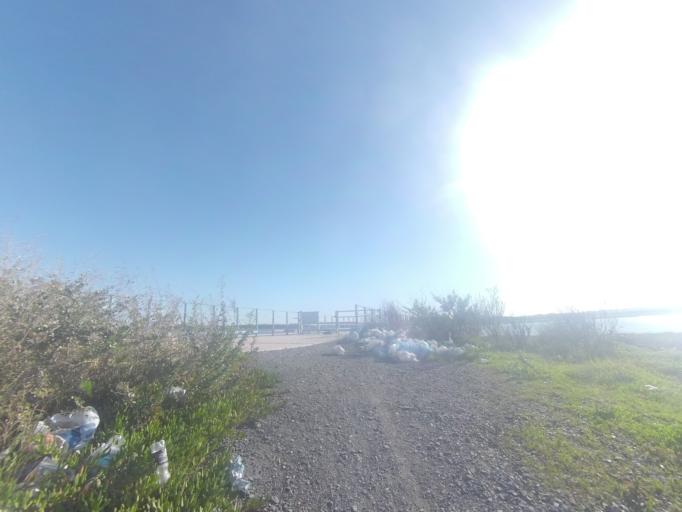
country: ES
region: Andalusia
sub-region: Provincia de Huelva
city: Palos de la Frontera
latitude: 37.2508
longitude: -6.9017
